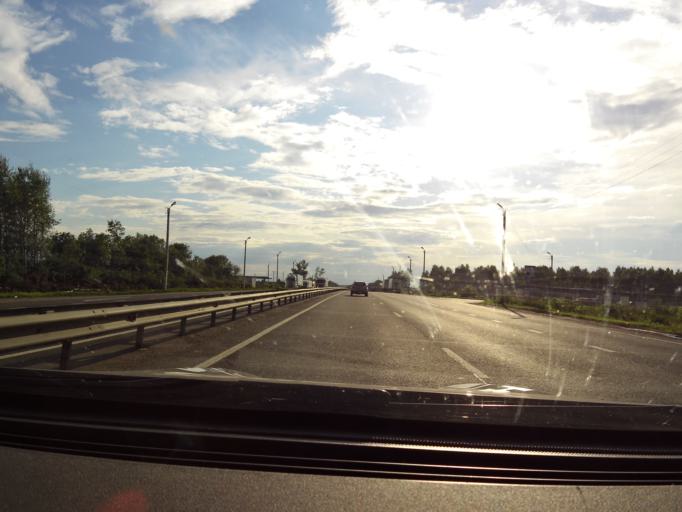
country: RU
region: Vladimir
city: Novki
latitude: 56.2034
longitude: 41.1371
